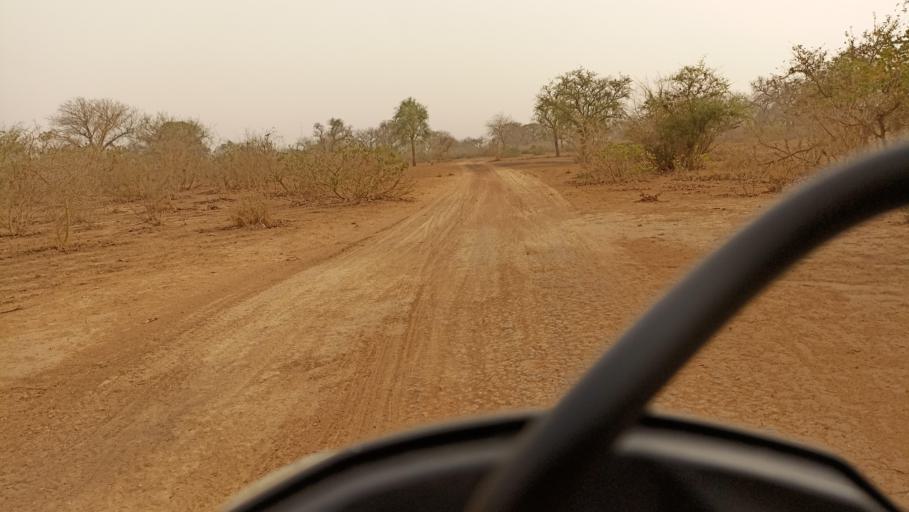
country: BF
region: Nord
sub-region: Province du Zondoma
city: Gourcy
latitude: 13.1671
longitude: -2.5893
